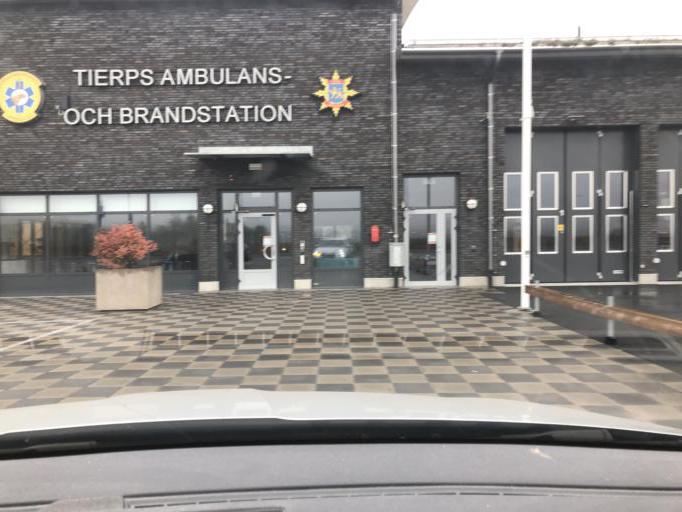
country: SE
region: Uppsala
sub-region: Tierps Kommun
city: Tierp
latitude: 60.3465
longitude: 17.4883
